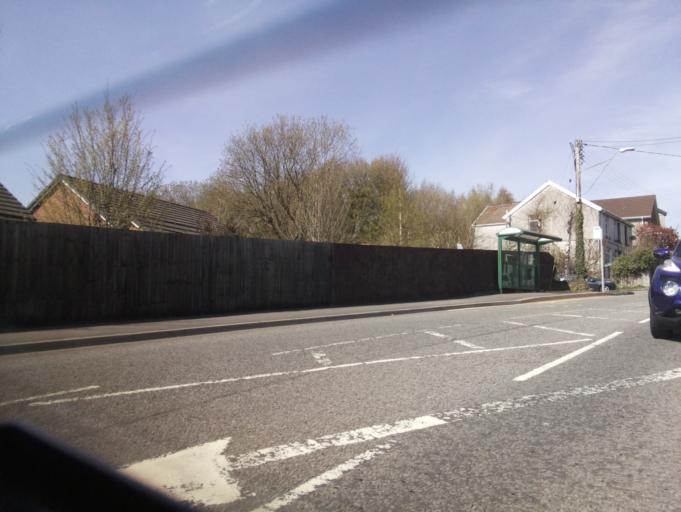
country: GB
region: Wales
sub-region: Rhondda Cynon Taf
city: Aberdare
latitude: 51.7274
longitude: -3.4568
